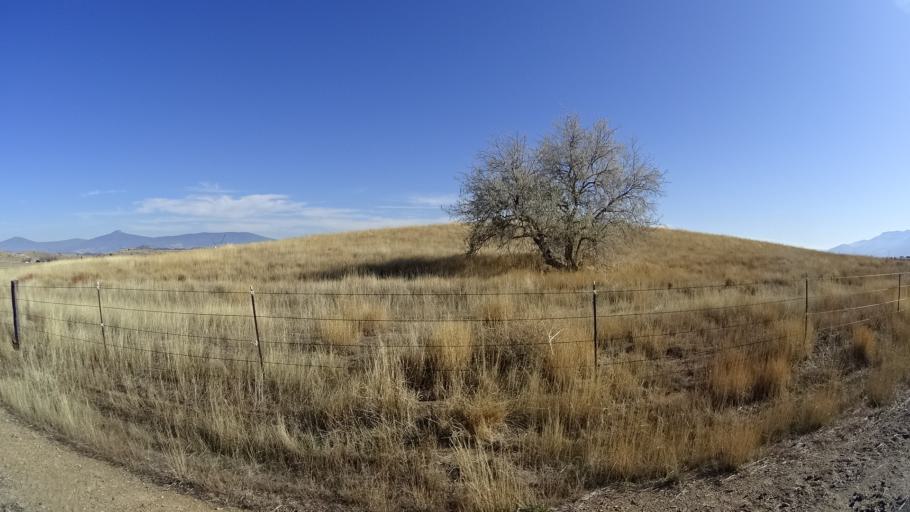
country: US
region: California
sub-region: Siskiyou County
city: Montague
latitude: 41.5726
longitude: -122.5484
